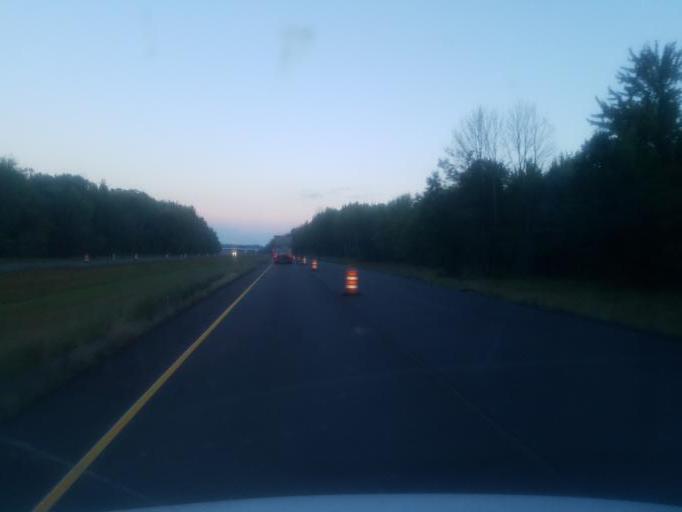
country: US
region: Ohio
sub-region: Ashtabula County
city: Jefferson
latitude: 41.7908
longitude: -80.7389
